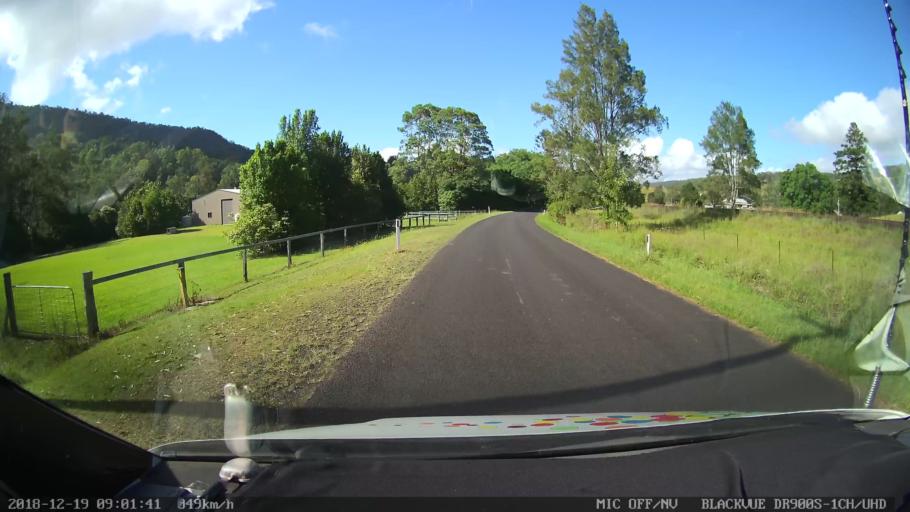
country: AU
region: New South Wales
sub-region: Kyogle
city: Kyogle
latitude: -28.4406
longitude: 152.9591
